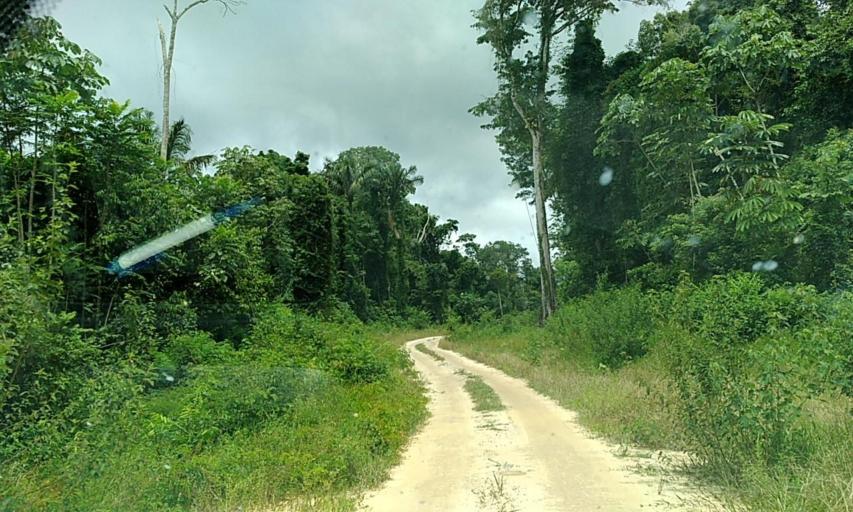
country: BR
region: Para
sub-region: Altamira
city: Altamira
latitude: -3.0631
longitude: -52.9088
